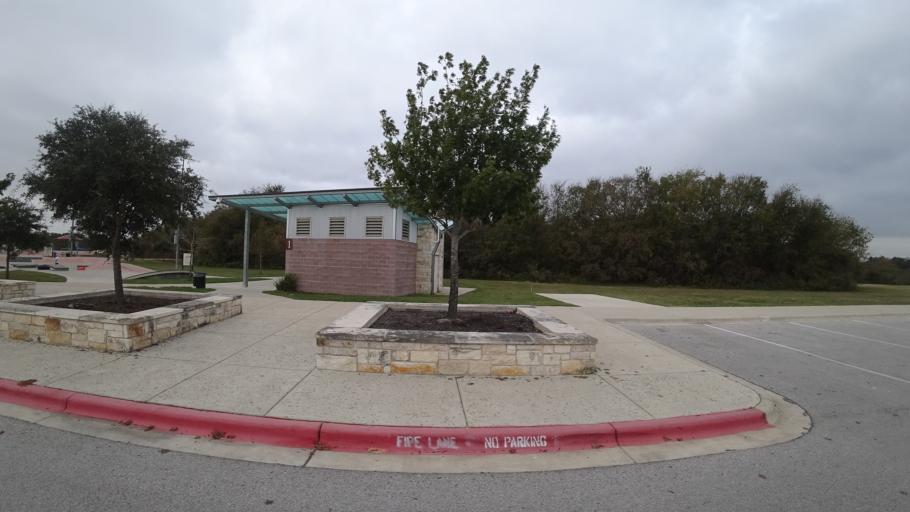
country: US
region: Texas
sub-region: Travis County
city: Pflugerville
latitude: 30.4066
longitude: -97.5974
